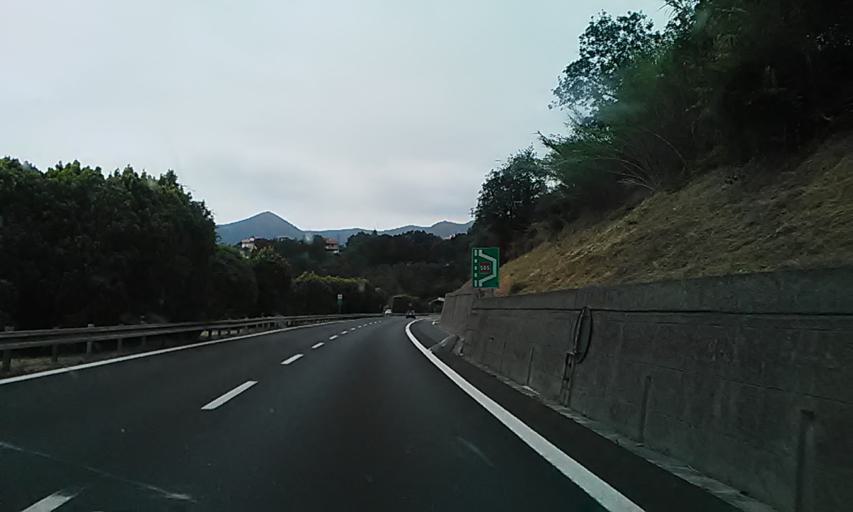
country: IT
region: Liguria
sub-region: Provincia di Savona
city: Boissano
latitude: 44.1336
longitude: 8.2383
